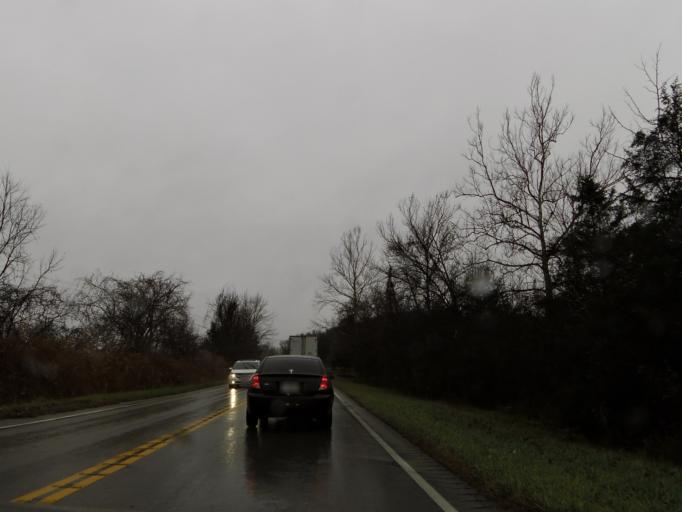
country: US
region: Kentucky
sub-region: Rockcastle County
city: Mount Vernon
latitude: 37.4219
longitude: -84.3336
